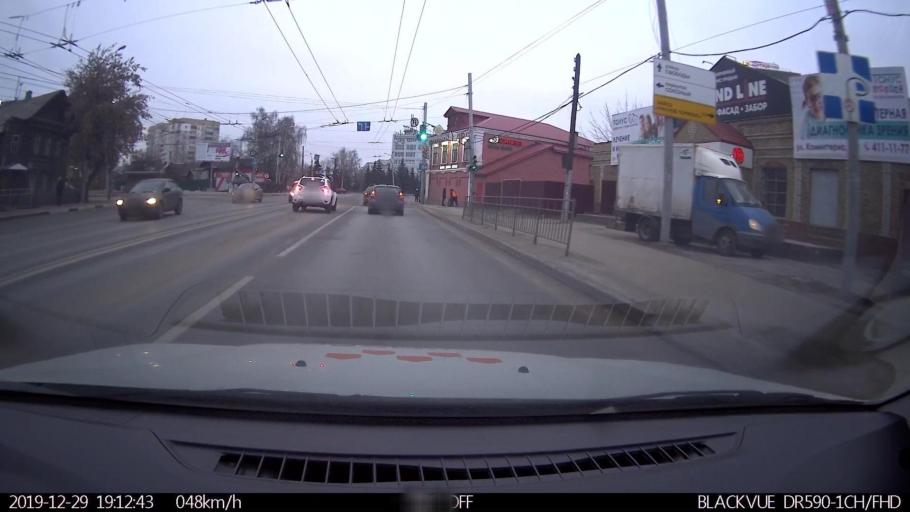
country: RU
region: Nizjnij Novgorod
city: Neklyudovo
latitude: 56.3607
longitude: 43.8626
